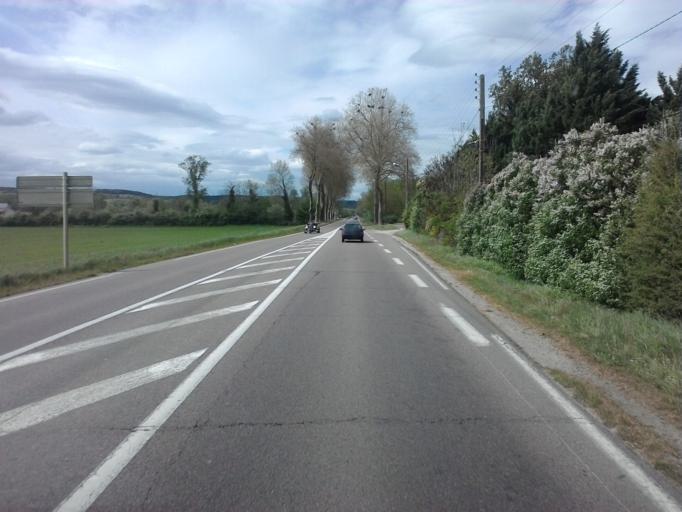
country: FR
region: Bourgogne
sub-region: Departement de l'Yonne
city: Champs-sur-Yonne
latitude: 47.7210
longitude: 3.6110
